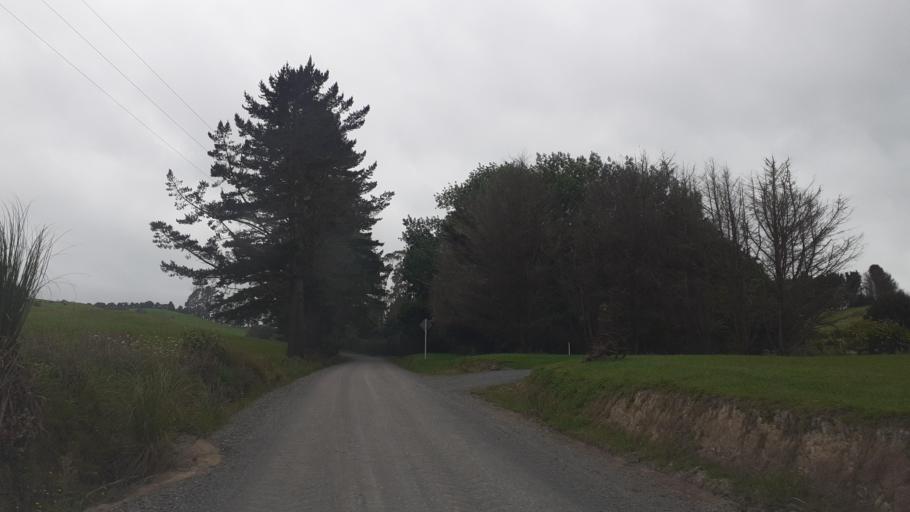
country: NZ
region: Northland
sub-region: Far North District
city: Kerikeri
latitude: -35.2820
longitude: 173.9577
